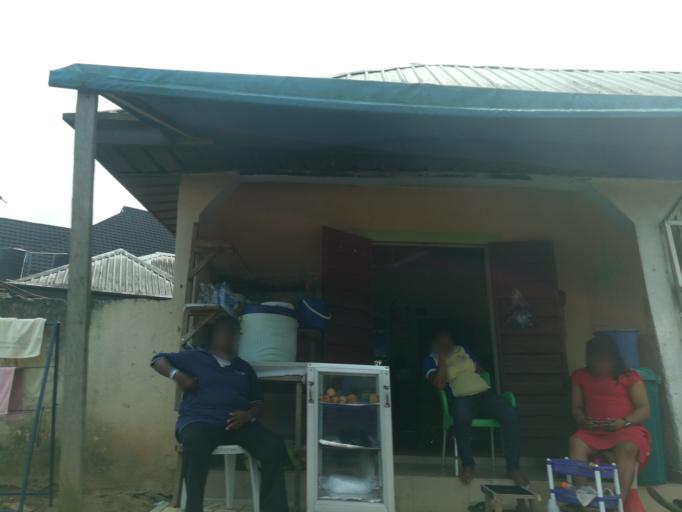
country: NG
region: Rivers
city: Port Harcourt
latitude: 4.8909
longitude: 6.9813
